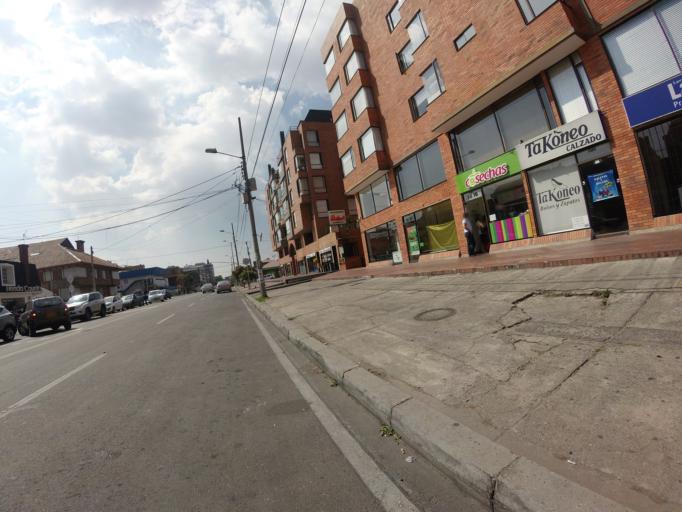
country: CO
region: Bogota D.C.
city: Barrio San Luis
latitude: 4.7048
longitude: -74.0501
